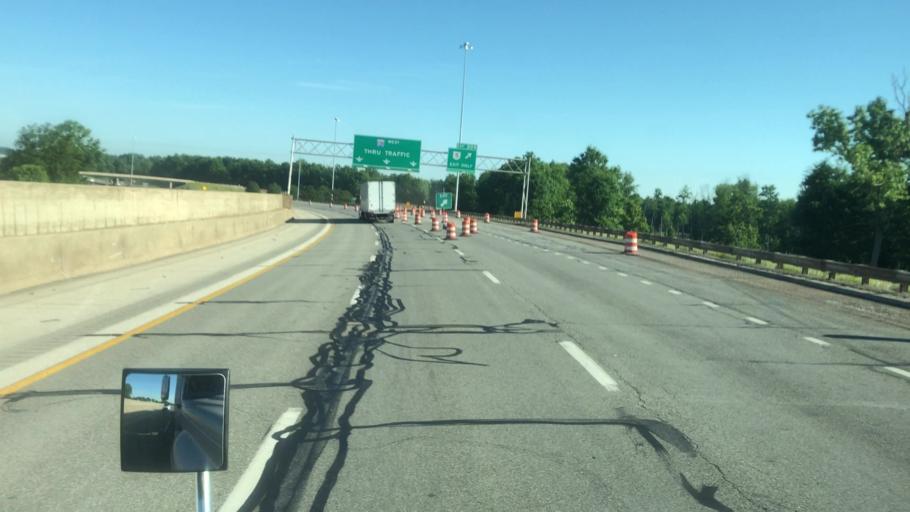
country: US
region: Ohio
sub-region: Trumbull County
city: Newton Falls
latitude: 41.2149
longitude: -80.9506
